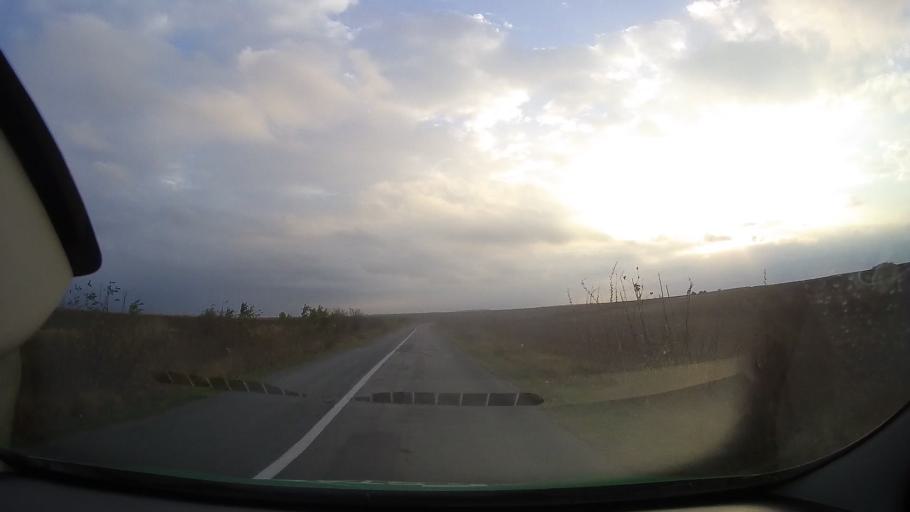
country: RO
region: Constanta
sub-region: Comuna Adamclisi
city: Adamclisi
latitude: 44.0196
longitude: 27.9061
